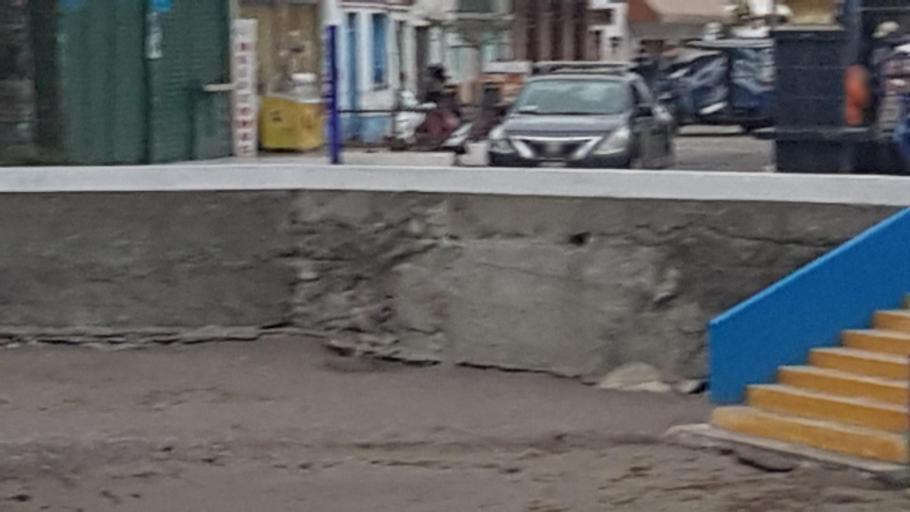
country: PE
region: Lima
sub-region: Lima
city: Pucusana
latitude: -12.4822
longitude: -76.8006
